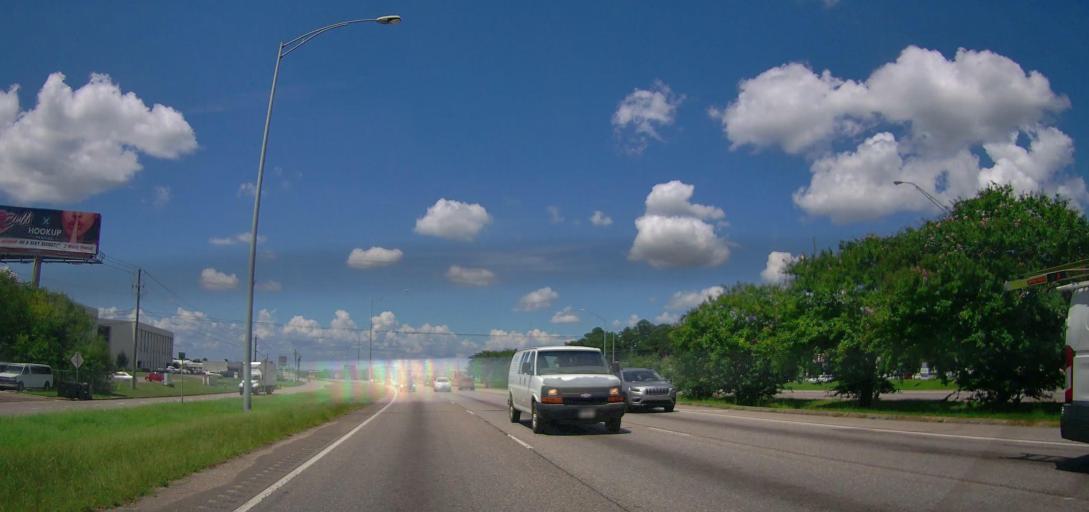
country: US
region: Alabama
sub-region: Montgomery County
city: Montgomery
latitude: 32.3715
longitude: -86.2096
